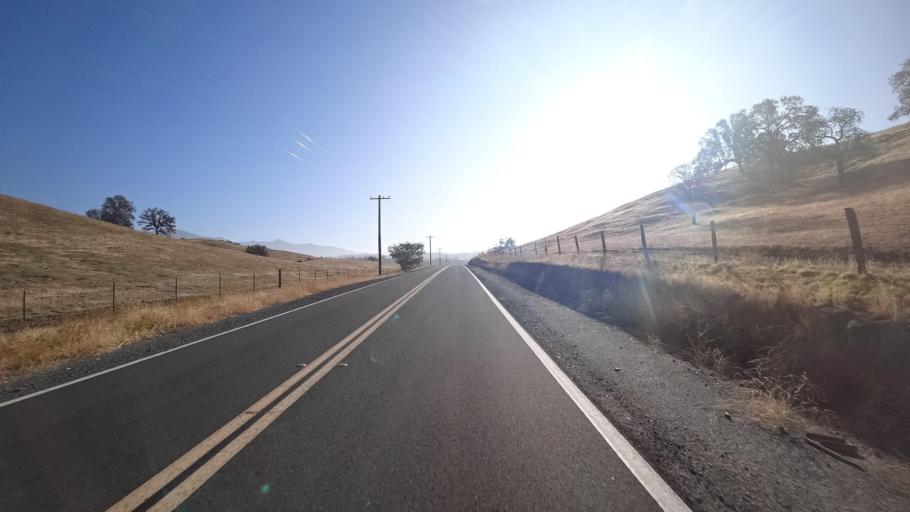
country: US
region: California
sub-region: Tulare County
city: Richgrove
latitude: 35.7390
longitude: -118.8654
